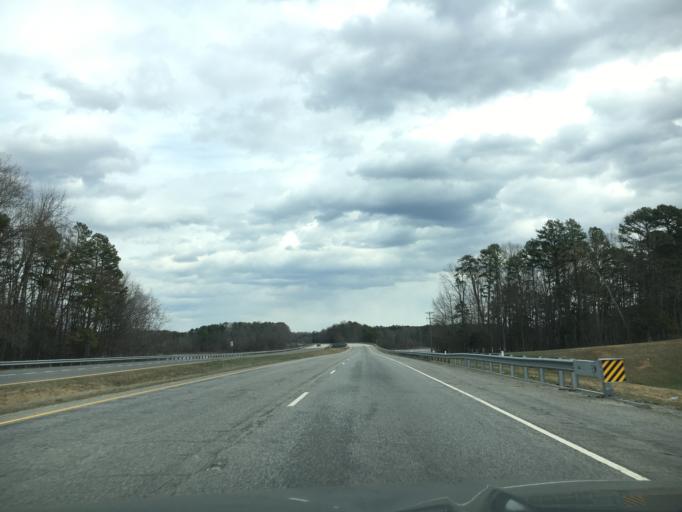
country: US
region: Virginia
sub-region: Mecklenburg County
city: Boydton
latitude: 36.6535
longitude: -78.4603
